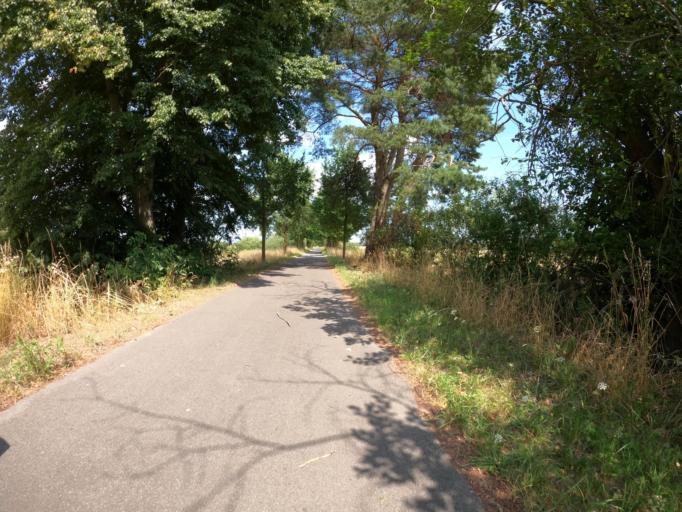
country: DE
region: Mecklenburg-Vorpommern
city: Woldegk
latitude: 53.3188
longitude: 13.5823
